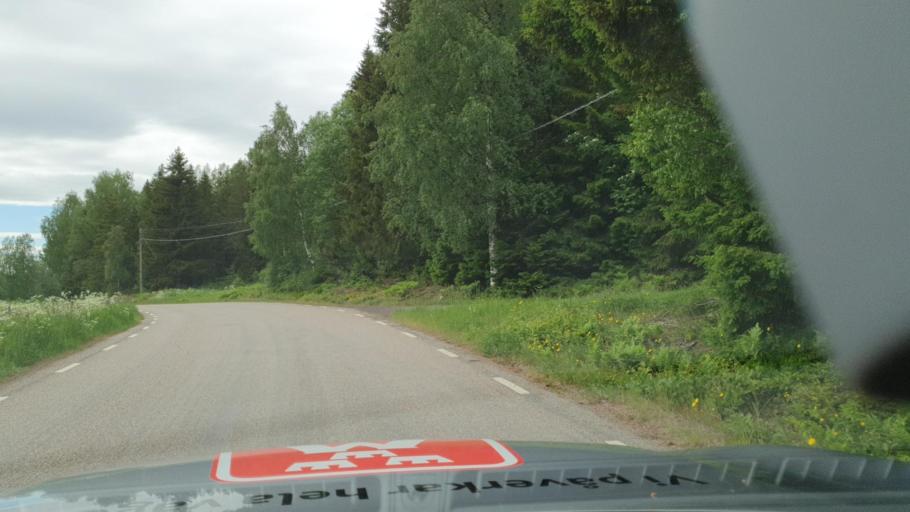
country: SE
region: Vaesternorrland
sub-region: Kramfors Kommun
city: Nordingra
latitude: 62.8939
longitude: 18.3726
